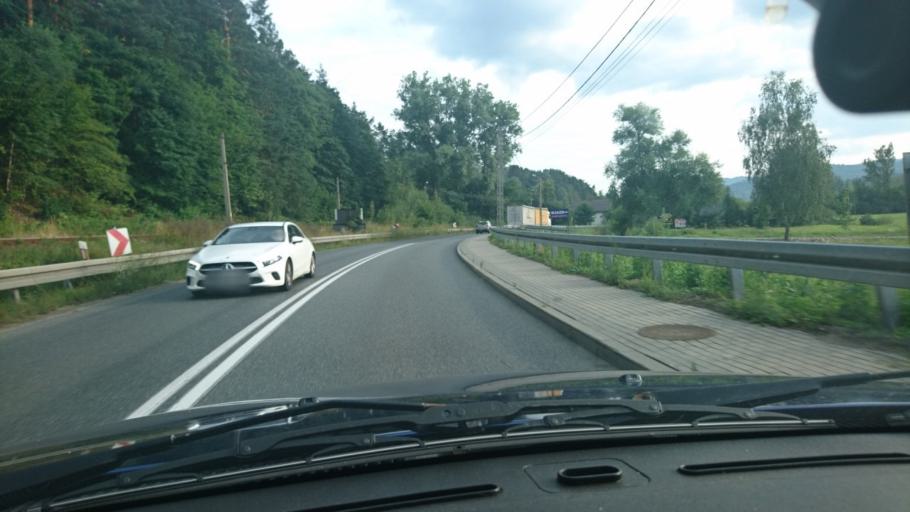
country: PL
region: Silesian Voivodeship
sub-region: Powiat zywiecki
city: Cisiec
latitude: 49.5759
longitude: 19.1012
